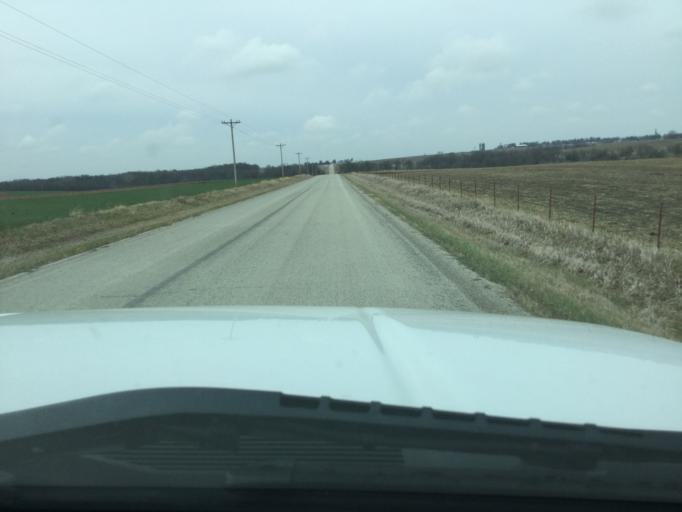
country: US
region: Kansas
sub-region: Nemaha County
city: Sabetha
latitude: 39.8616
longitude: -95.7142
